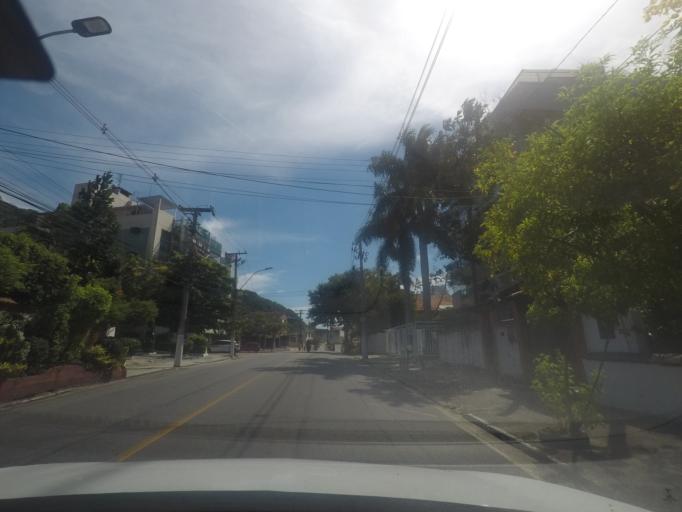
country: BR
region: Rio de Janeiro
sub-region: Niteroi
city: Niteroi
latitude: -22.9188
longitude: -43.0871
